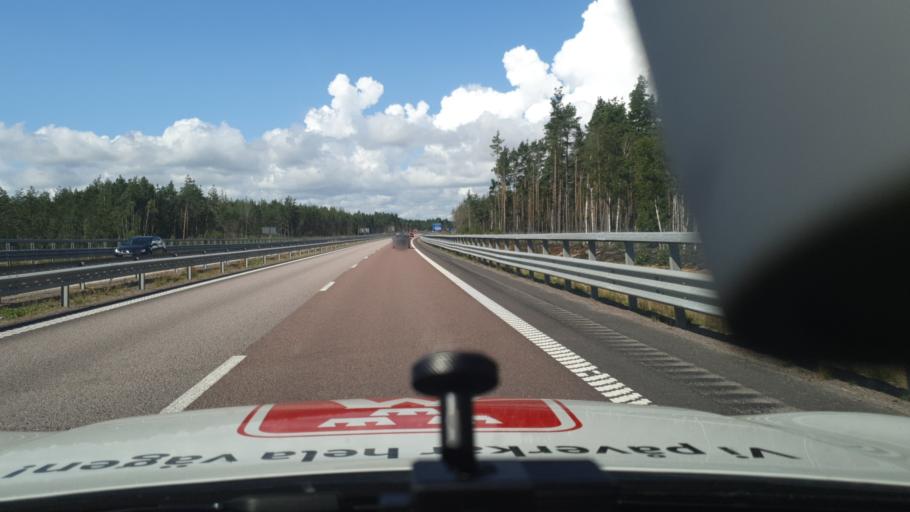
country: SE
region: Vaermland
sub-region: Kils Kommun
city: Kil
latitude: 59.3858
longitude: 13.3145
